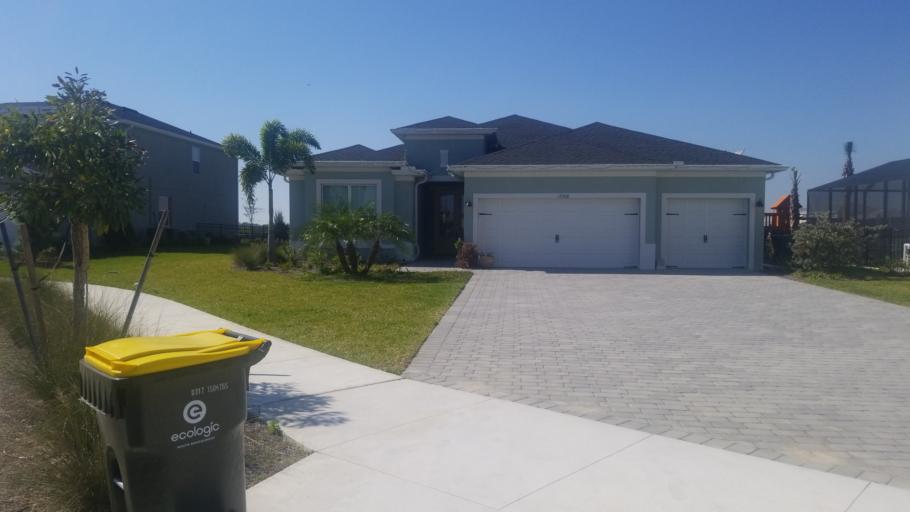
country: US
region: Florida
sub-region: Lee County
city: Olga
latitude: 26.7748
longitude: -81.7401
